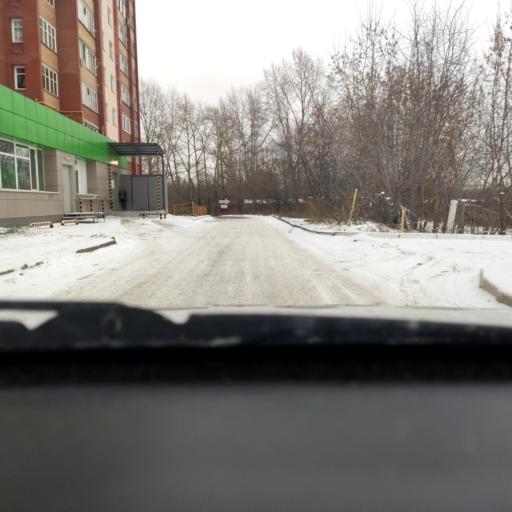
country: RU
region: Perm
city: Kondratovo
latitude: 58.0318
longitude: 56.0284
